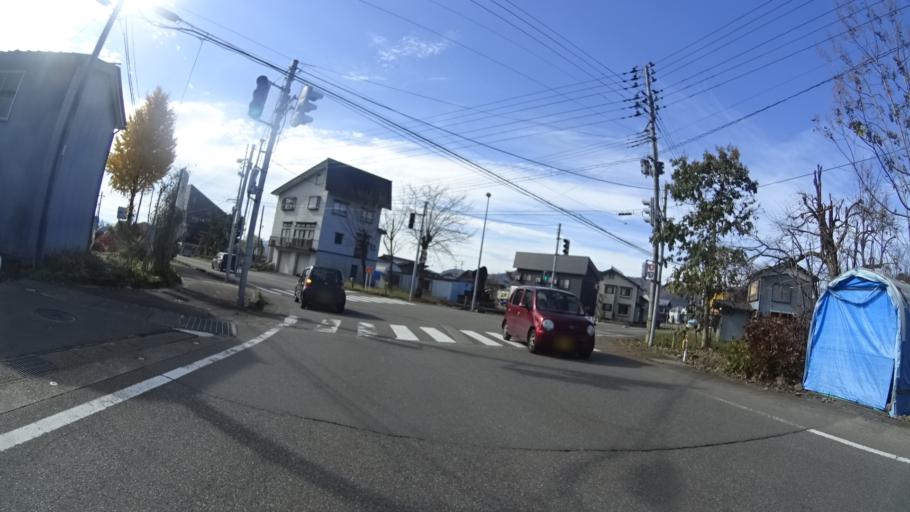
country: JP
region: Niigata
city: Ojiya
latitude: 37.2561
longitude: 138.9819
